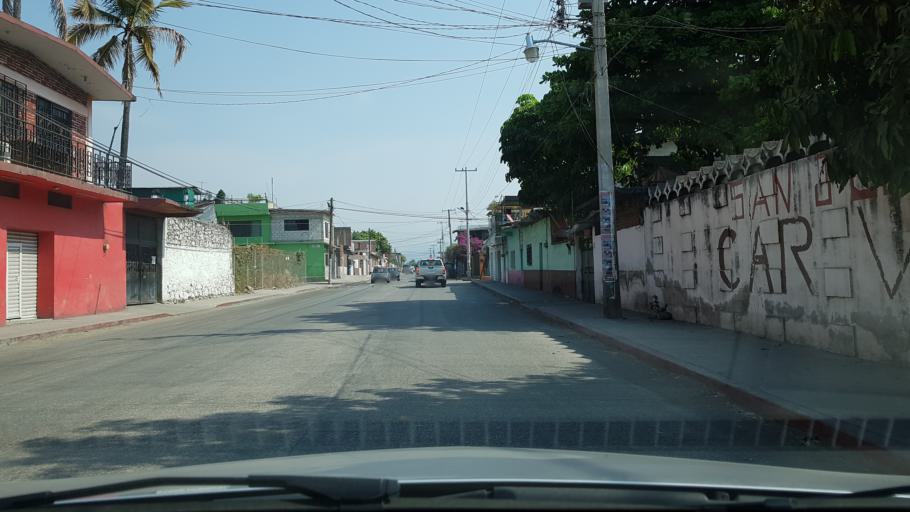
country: MX
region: Morelos
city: Zacatepec
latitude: 18.6604
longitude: -99.1863
